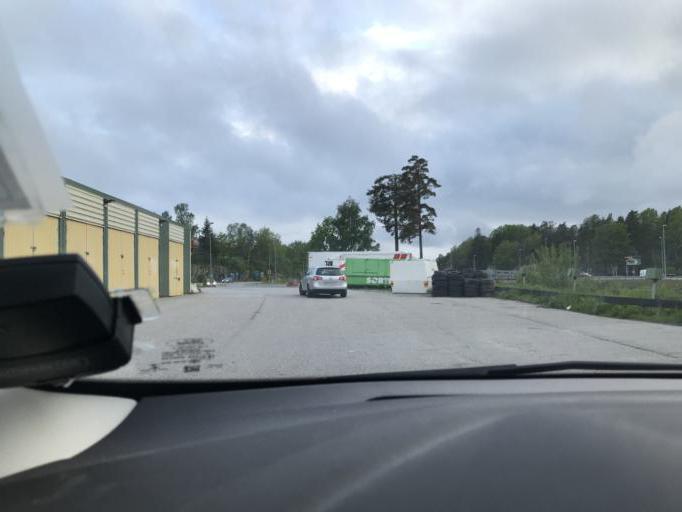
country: SE
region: Stockholm
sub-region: Botkyrka Kommun
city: Tullinge
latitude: 59.2094
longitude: 17.9209
